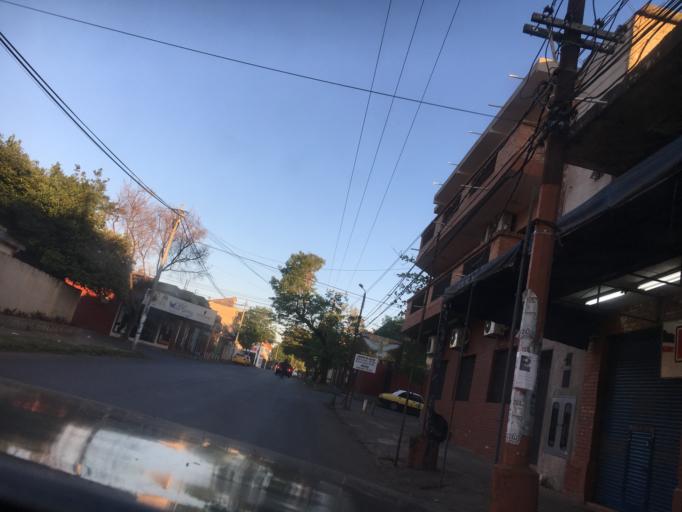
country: PY
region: Asuncion
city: Asuncion
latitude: -25.3162
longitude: -57.6180
